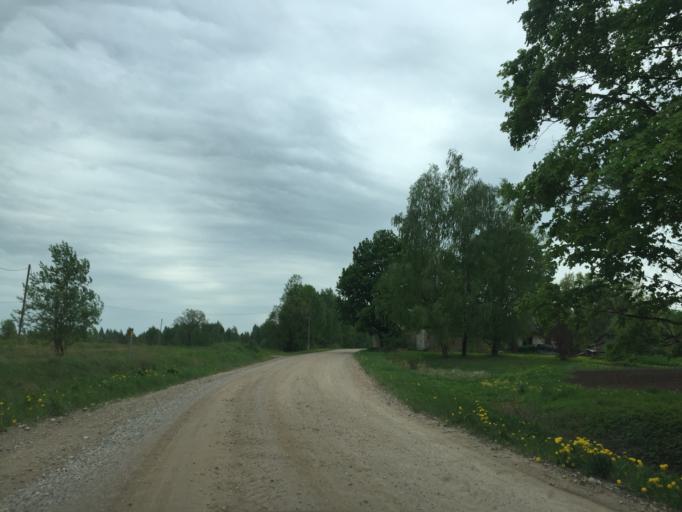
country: LV
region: Lielvarde
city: Lielvarde
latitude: 56.8042
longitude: 24.8621
